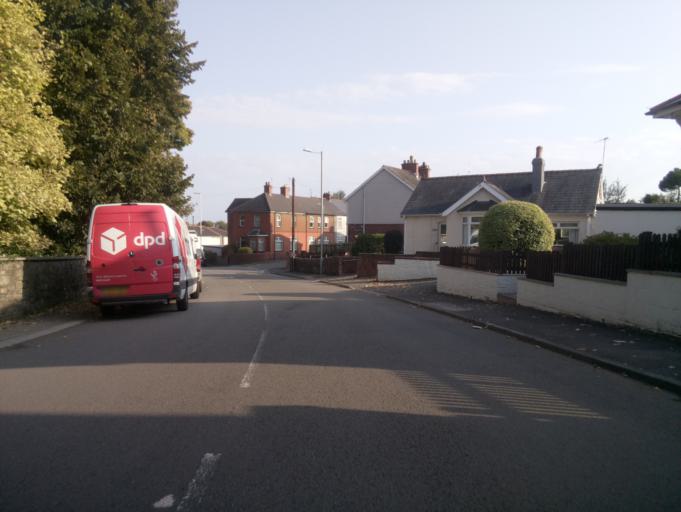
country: GB
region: Wales
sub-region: Torfaen County Borough
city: New Inn
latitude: 51.6901
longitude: -3.0276
